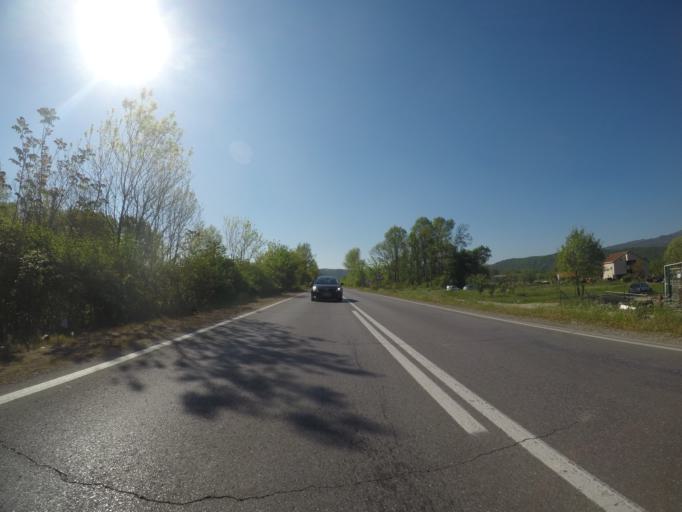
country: ME
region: Danilovgrad
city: Danilovgrad
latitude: 42.5266
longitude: 19.1181
